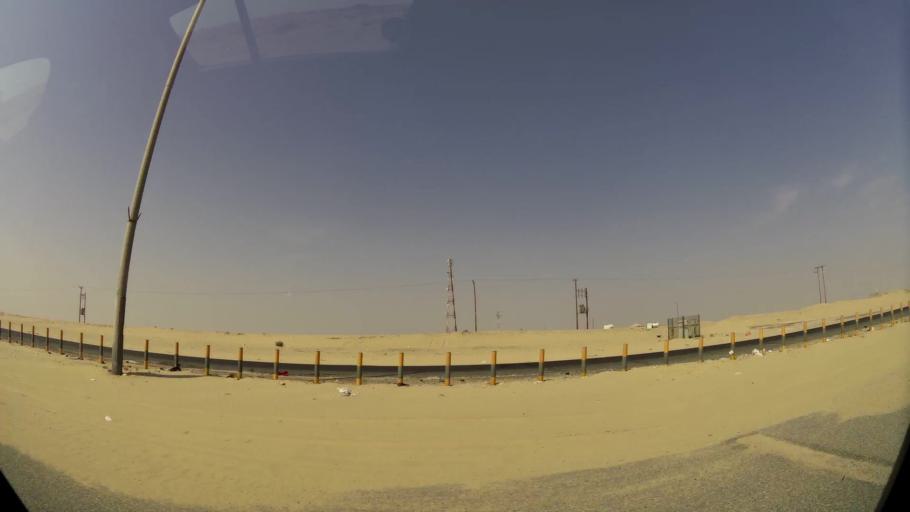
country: KW
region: Al Ahmadi
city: Al Ahmadi
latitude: 28.8423
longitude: 48.0600
